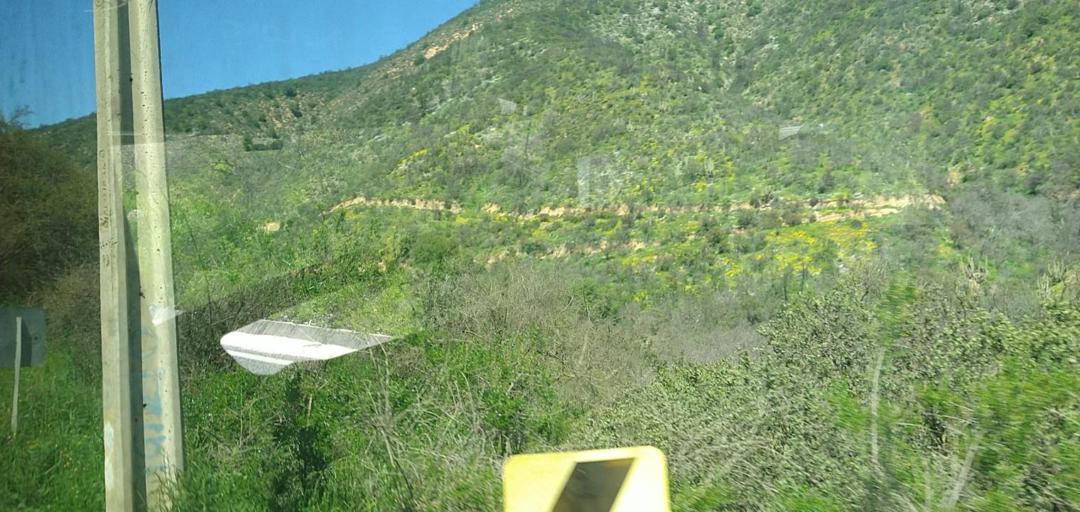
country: CL
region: Valparaiso
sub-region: Provincia de Marga Marga
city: Limache
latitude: -33.1946
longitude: -71.2765
